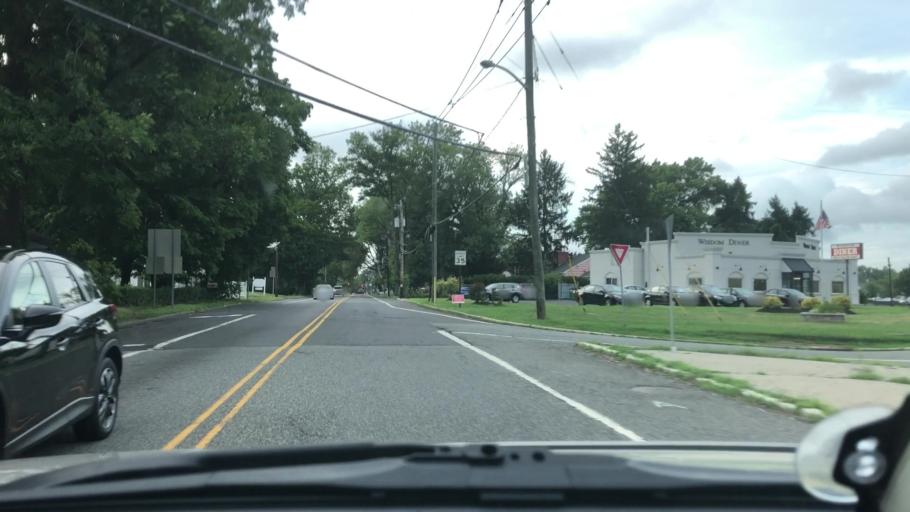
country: US
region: New Jersey
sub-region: Burlington County
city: Bordentown
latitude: 40.1366
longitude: -74.7043
